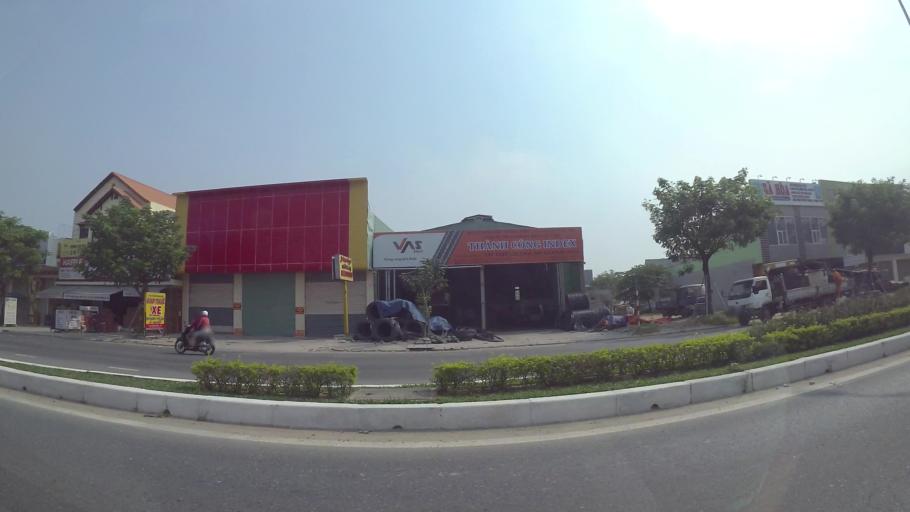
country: VN
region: Da Nang
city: Cam Le
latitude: 16.0054
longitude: 108.2213
